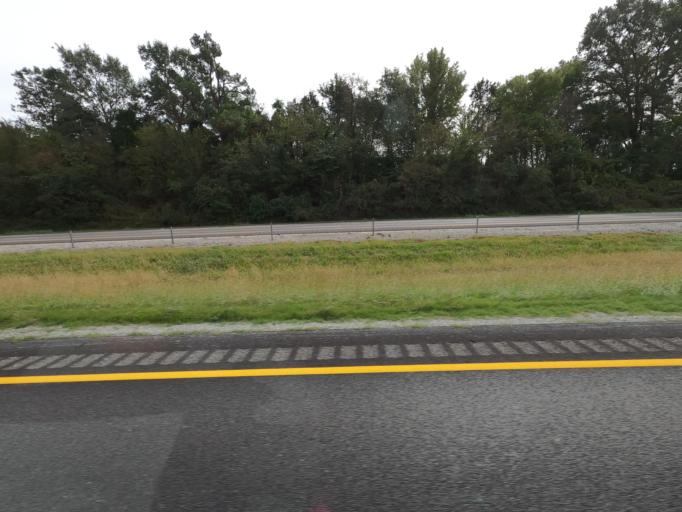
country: US
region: Tennessee
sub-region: Crockett County
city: Bells
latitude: 35.6040
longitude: -89.0372
